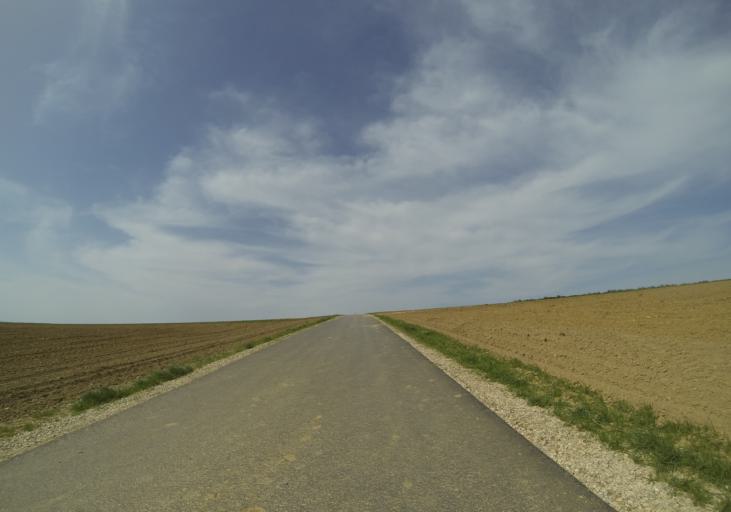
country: DE
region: Baden-Wuerttemberg
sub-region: Tuebingen Region
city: Burgrieden
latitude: 48.2482
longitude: 9.9296
